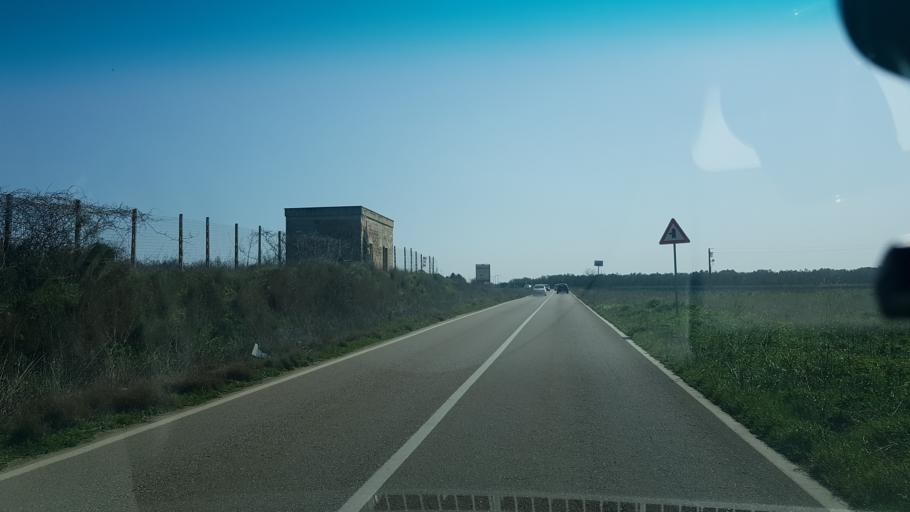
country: IT
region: Apulia
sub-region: Provincia di Brindisi
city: Torchiarolo
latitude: 40.5117
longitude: 18.0878
